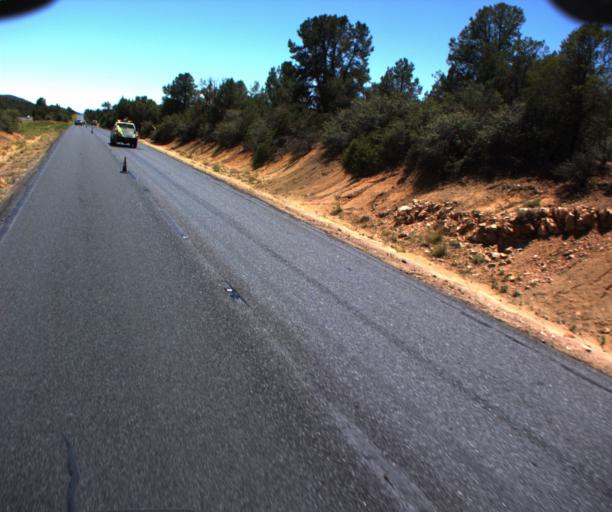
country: US
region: Arizona
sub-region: Gila County
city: Payson
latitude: 34.2141
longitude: -111.3320
